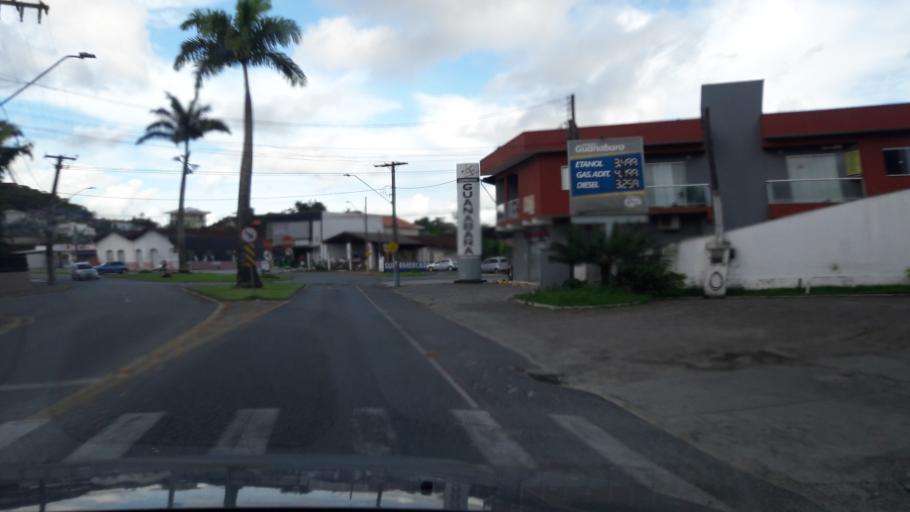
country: BR
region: Santa Catarina
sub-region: Joinville
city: Joinville
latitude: -26.3258
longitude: -48.8314
